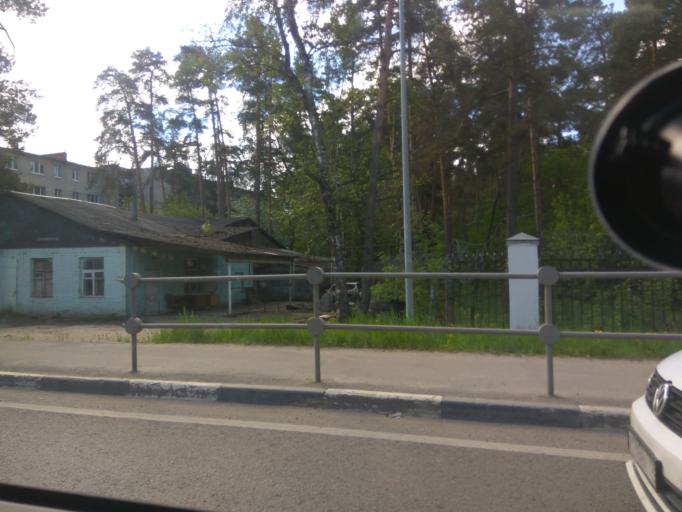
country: RU
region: Moskovskaya
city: Zhukovskiy
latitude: 55.5803
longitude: 38.1316
